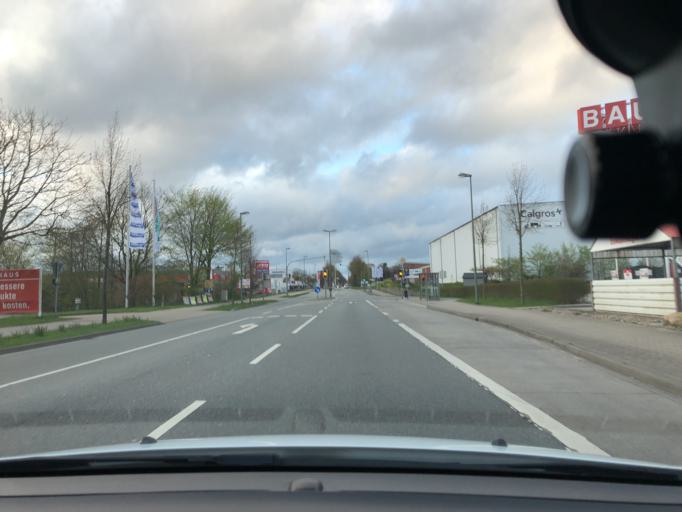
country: DE
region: Schleswig-Holstein
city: Flensburg
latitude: 54.7645
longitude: 9.4352
